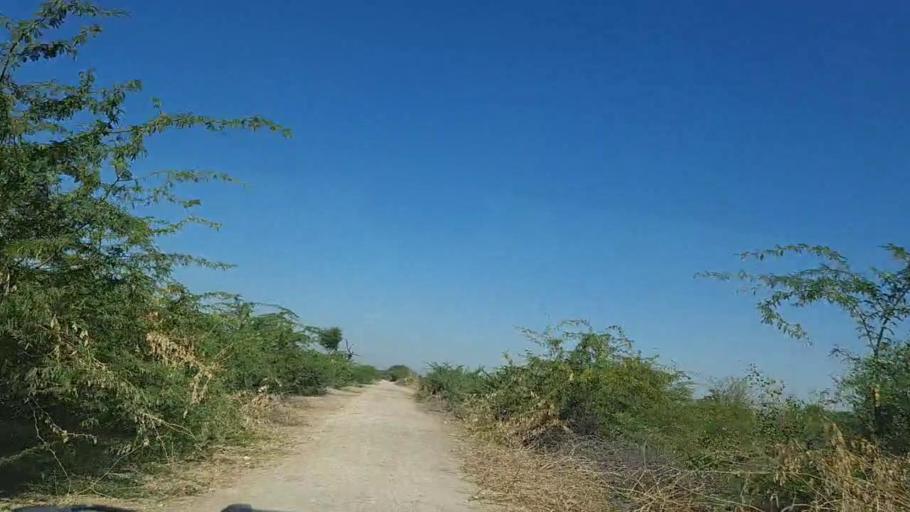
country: PK
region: Sindh
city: Dhoro Naro
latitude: 25.4637
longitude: 69.5133
